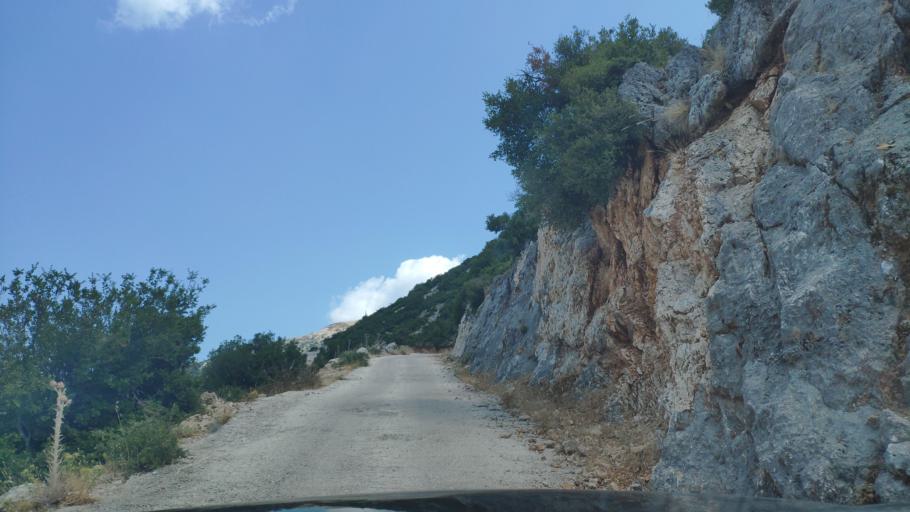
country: GR
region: West Greece
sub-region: Nomos Aitolias kai Akarnanias
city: Monastirakion
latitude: 38.7800
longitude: 20.9757
